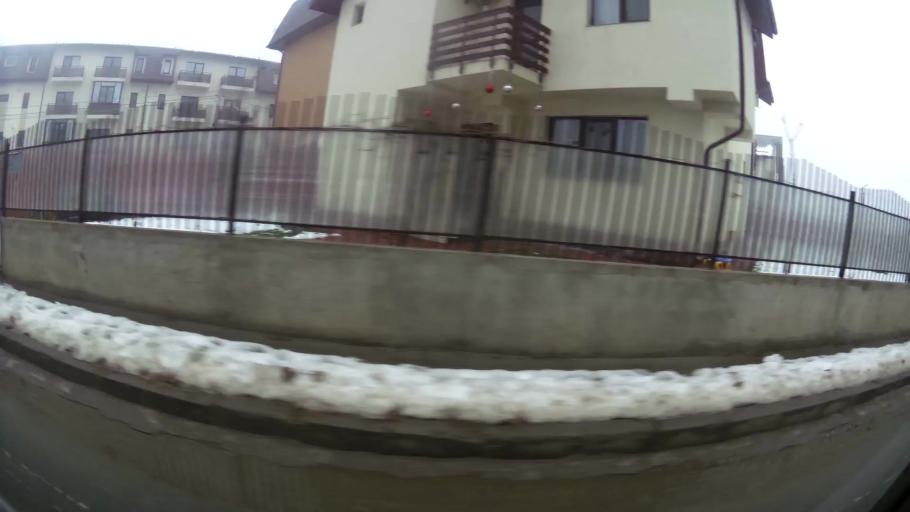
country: RO
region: Ilfov
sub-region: Comuna Chiajna
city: Rosu
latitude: 44.4567
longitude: 25.9933
